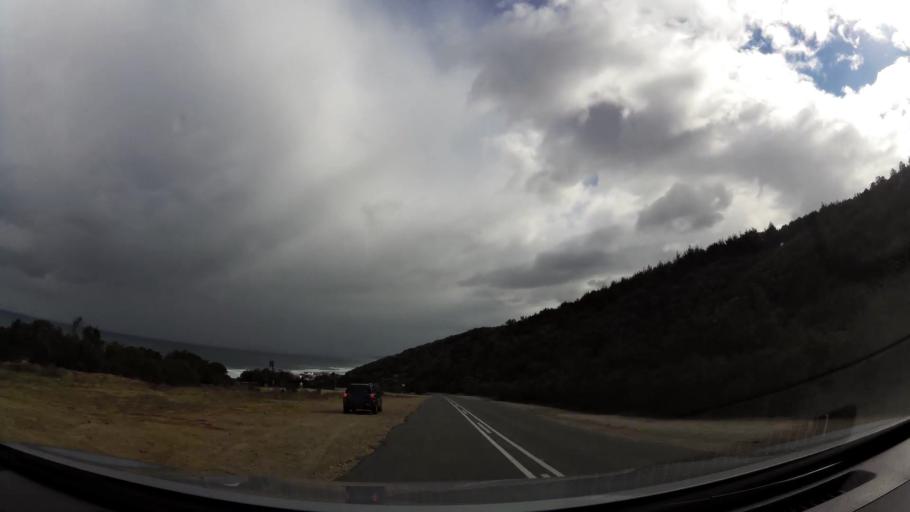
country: ZA
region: Western Cape
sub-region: Eden District Municipality
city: George
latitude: -34.0460
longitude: 22.3147
